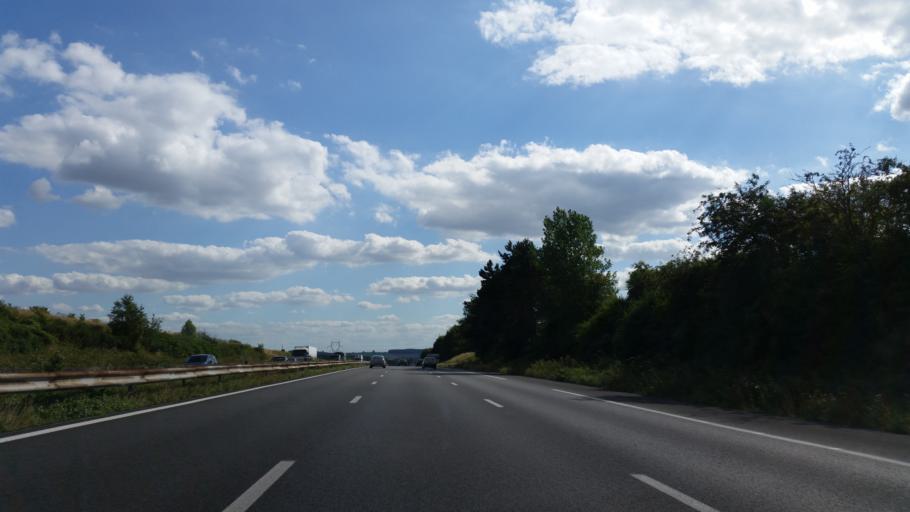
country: FR
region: Picardie
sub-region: Departement de la Somme
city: Peronne
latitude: 49.9845
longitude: 2.8696
